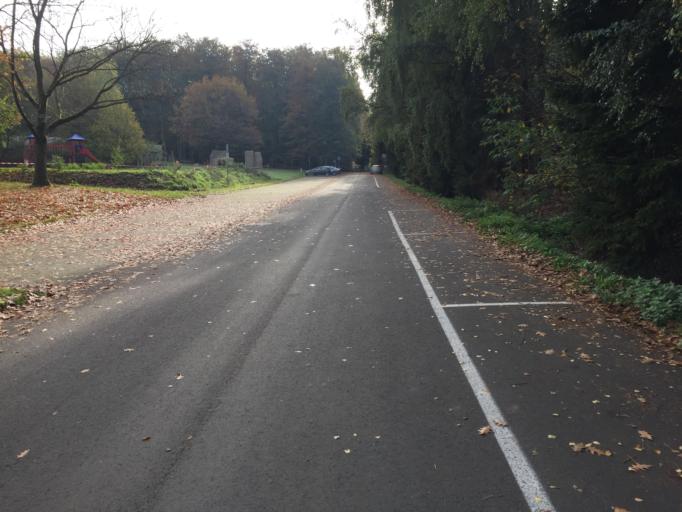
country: DE
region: Hesse
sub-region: Regierungsbezirk Giessen
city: Grunberg
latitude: 50.5879
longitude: 8.9852
